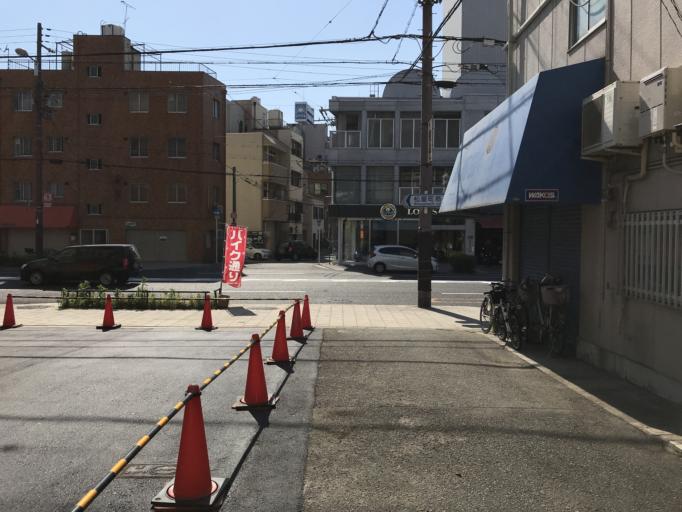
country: JP
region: Osaka
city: Osaka-shi
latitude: 34.6555
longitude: 135.5103
